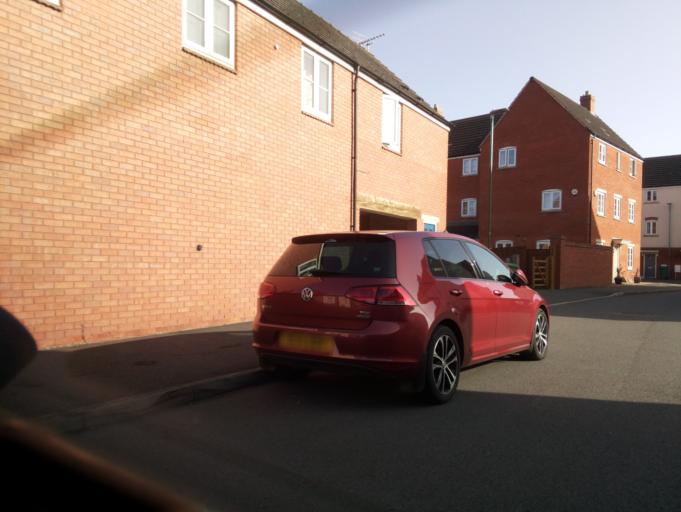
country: GB
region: England
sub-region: Gloucestershire
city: Tewkesbury
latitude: 51.9805
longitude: -2.1391
